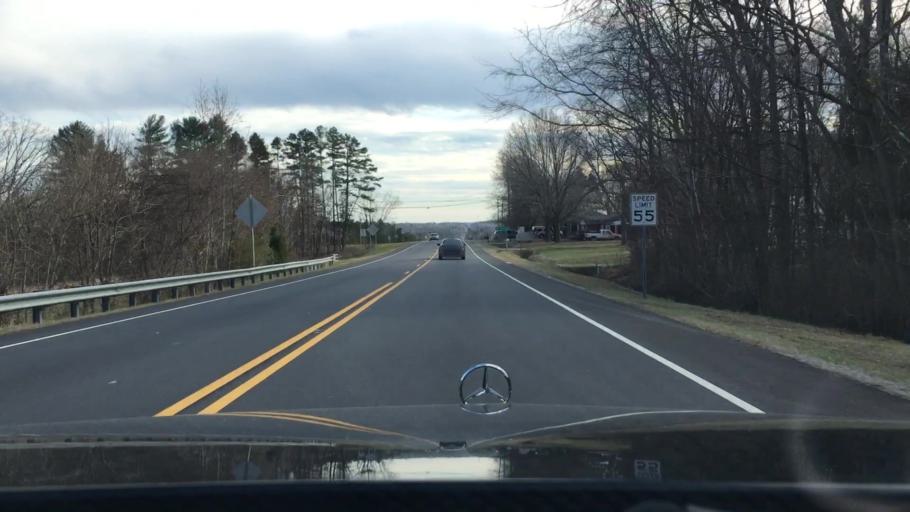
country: US
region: Virginia
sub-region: City of Danville
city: Danville
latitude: 36.5257
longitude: -79.3970
